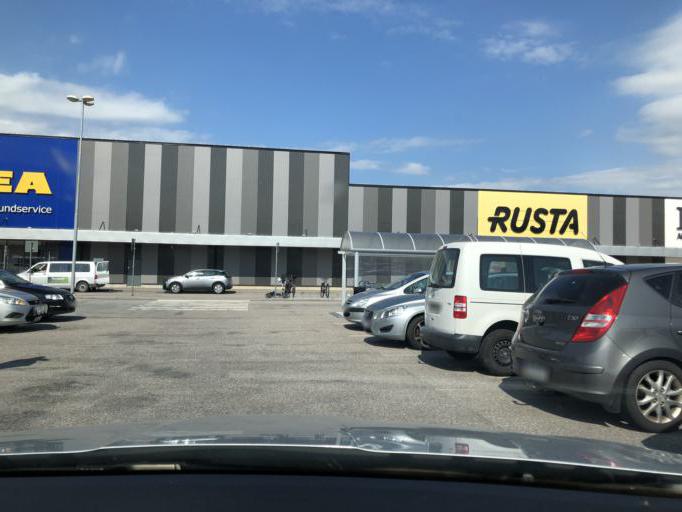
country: SE
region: Gaevleborg
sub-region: Gavle Kommun
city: Valbo
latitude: 60.6331
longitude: 16.9908
